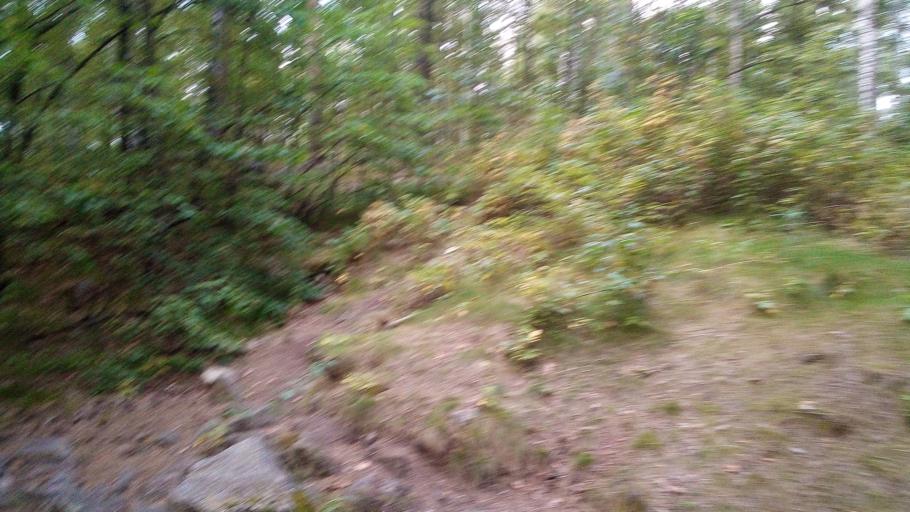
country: RU
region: Chelyabinsk
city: Turgoyak
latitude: 55.1611
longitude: 60.0318
